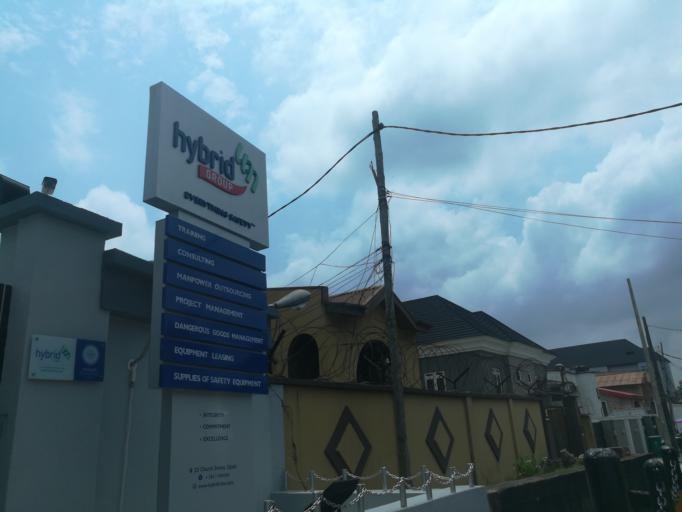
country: NG
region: Lagos
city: Ojota
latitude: 6.5933
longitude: 3.3632
